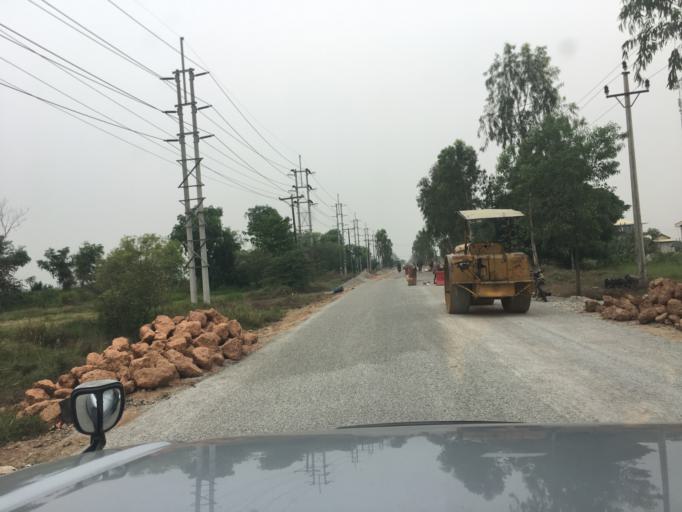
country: MM
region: Yangon
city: Syriam
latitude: 16.9527
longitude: 96.2725
